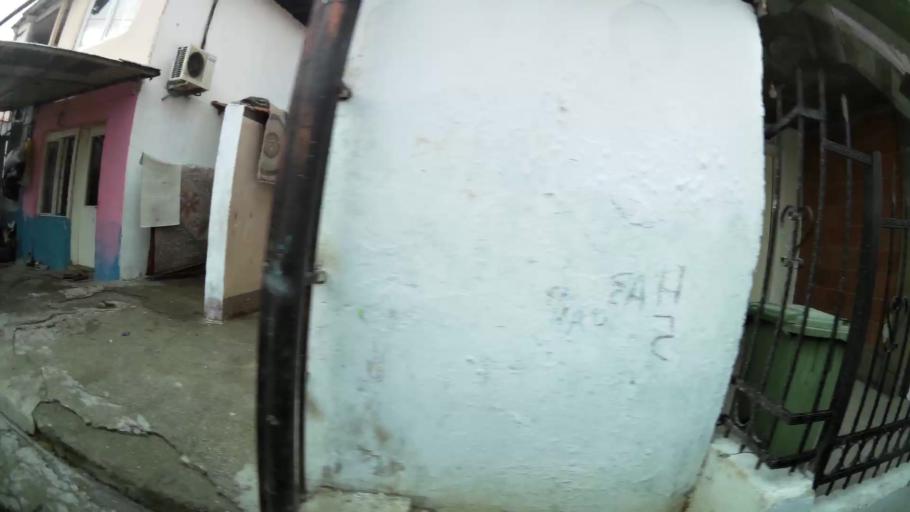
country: MK
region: Suto Orizari
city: Suto Orizare
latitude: 42.0450
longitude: 21.4211
